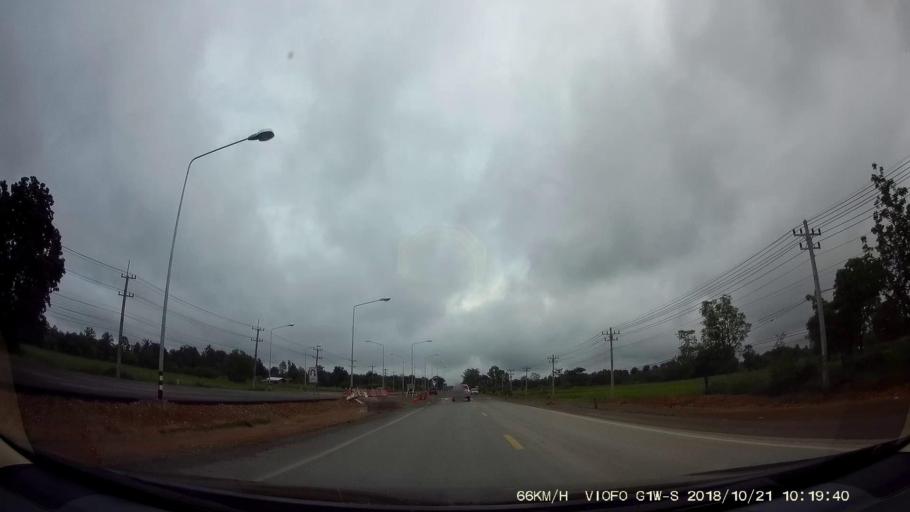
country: TH
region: Chaiyaphum
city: Phu Khiao
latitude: 16.3126
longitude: 102.2001
